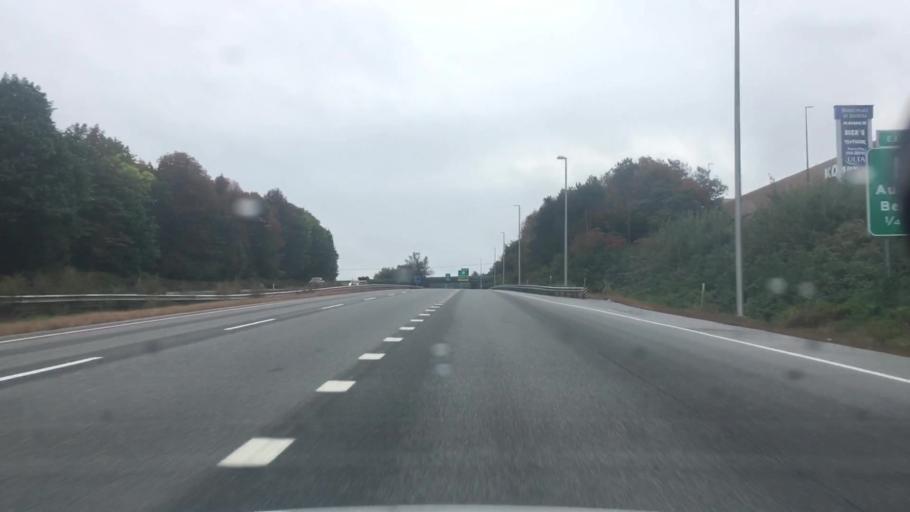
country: US
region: Maine
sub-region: Kennebec County
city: Augusta
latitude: 44.3496
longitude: -69.7878
